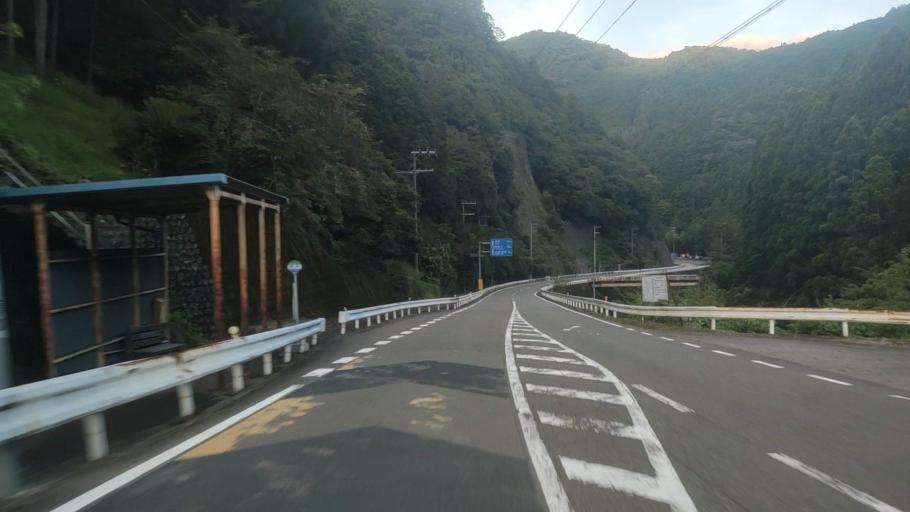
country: JP
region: Wakayama
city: Shingu
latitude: 33.8070
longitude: 135.7313
